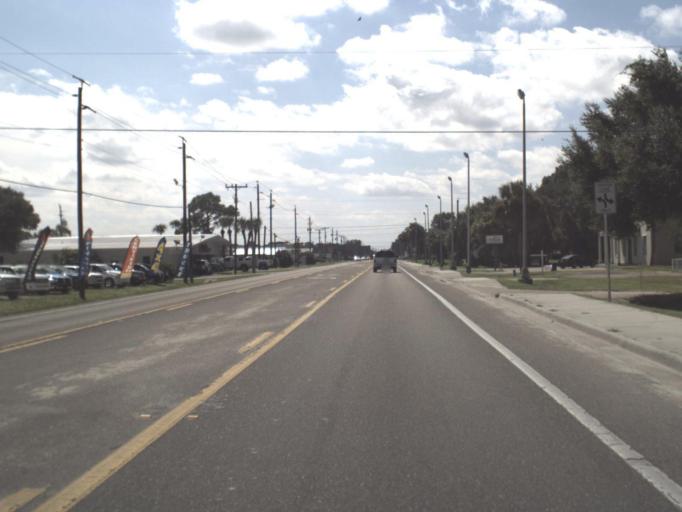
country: US
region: Florida
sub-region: Hendry County
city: LaBelle
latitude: 26.7545
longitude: -81.4383
